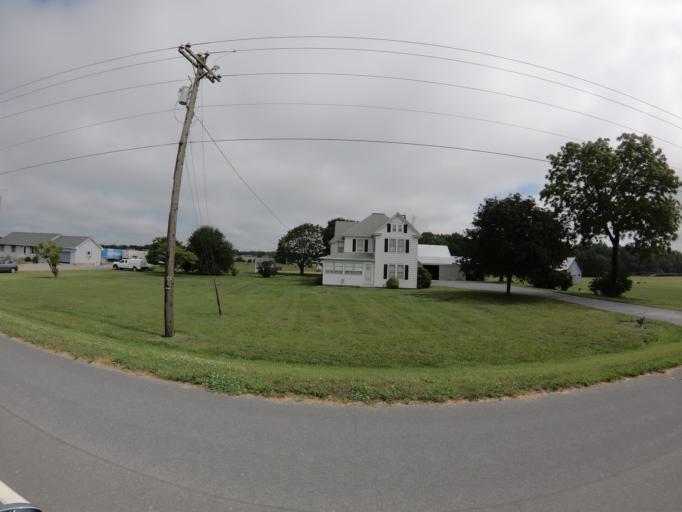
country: US
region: Delaware
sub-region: Kent County
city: Felton
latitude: 39.0067
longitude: -75.5513
